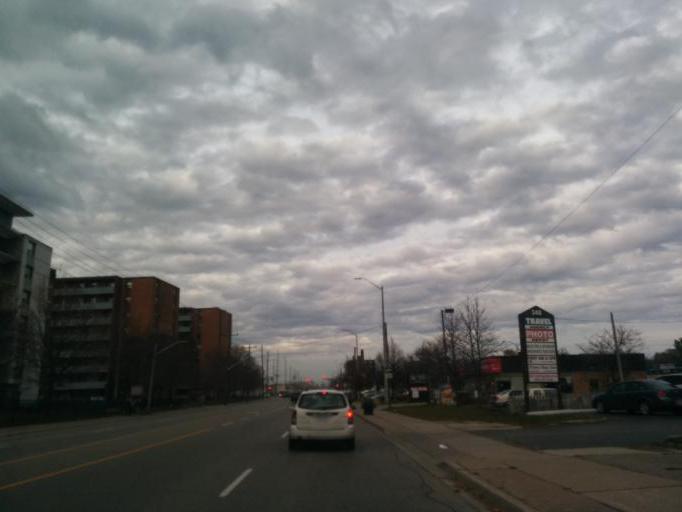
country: CA
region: Ontario
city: Mississauga
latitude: 43.5628
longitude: -79.5736
